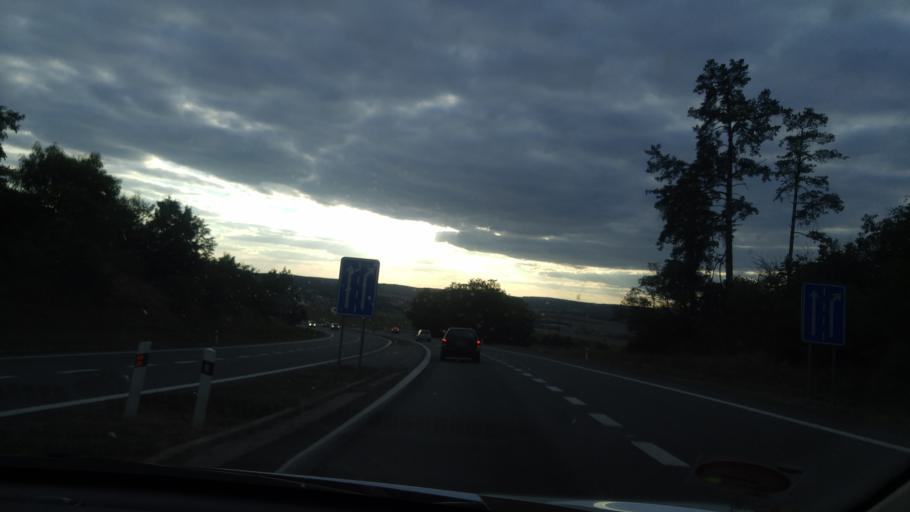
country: CZ
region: South Moravian
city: Ricany
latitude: 49.1932
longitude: 16.4283
